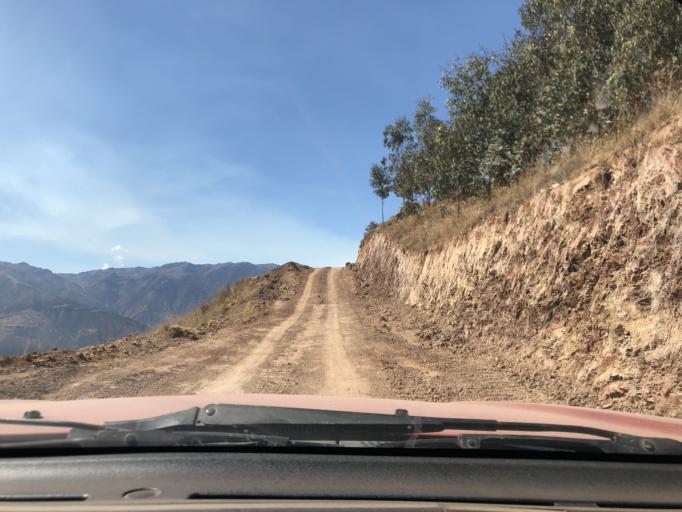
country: PE
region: Ayacucho
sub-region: Provincia de La Mar
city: Chilcas
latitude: -13.1815
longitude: -73.8414
